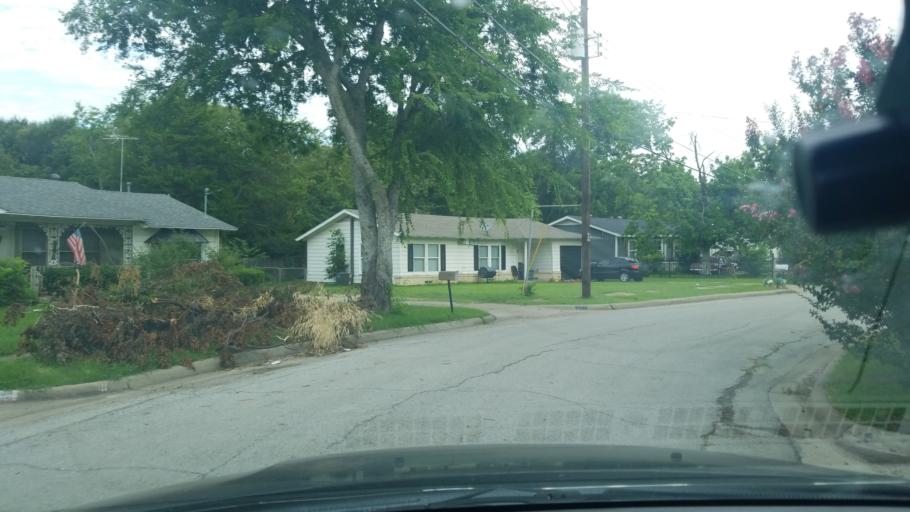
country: US
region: Texas
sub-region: Dallas County
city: Balch Springs
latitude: 32.7380
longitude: -96.6606
